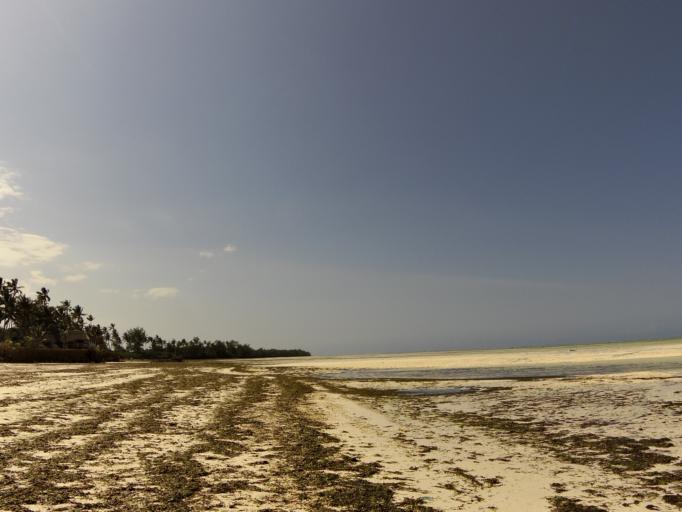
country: TZ
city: Kiwengwa
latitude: -6.0891
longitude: 39.4263
